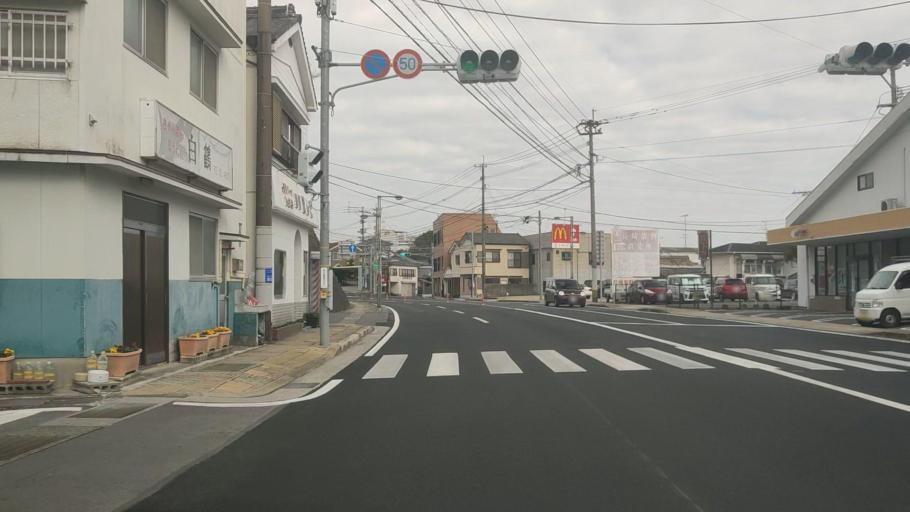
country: JP
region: Nagasaki
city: Shimabara
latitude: 32.7702
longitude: 130.3728
